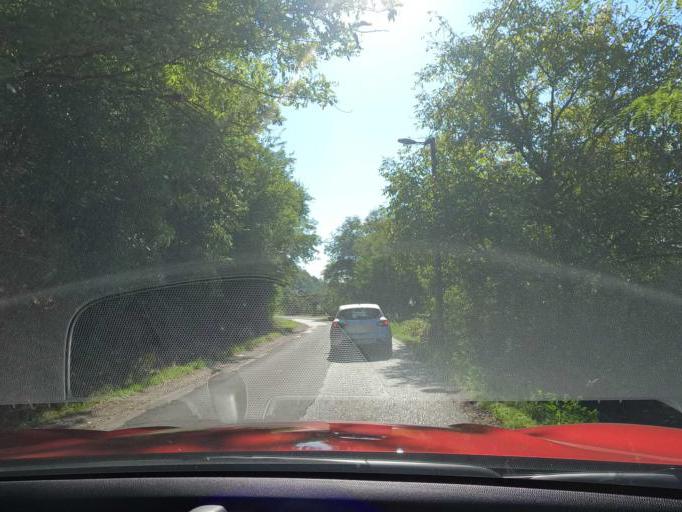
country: RS
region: Central Serbia
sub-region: Raski Okrug
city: Kraljevo
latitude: 43.7365
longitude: 20.7399
